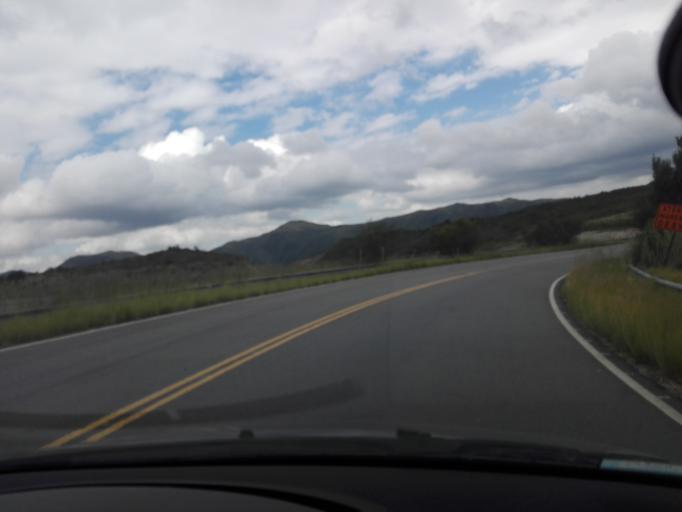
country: AR
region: Cordoba
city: Cuesta Blanca
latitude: -31.5685
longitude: -64.5879
